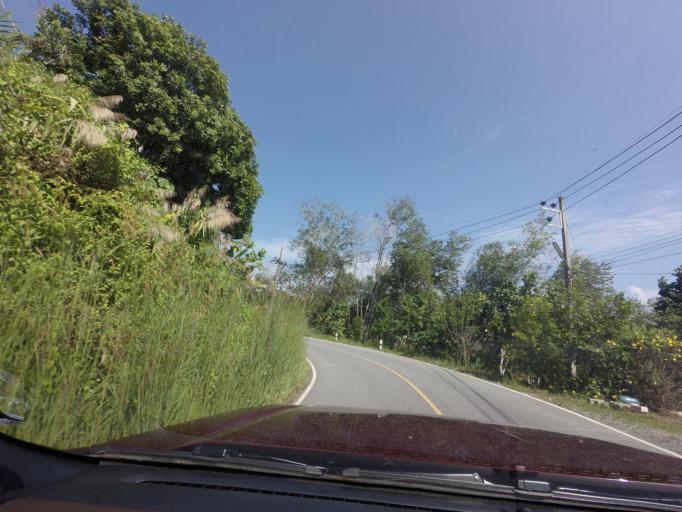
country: TH
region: Yala
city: Than To
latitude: 6.0084
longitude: 101.2242
